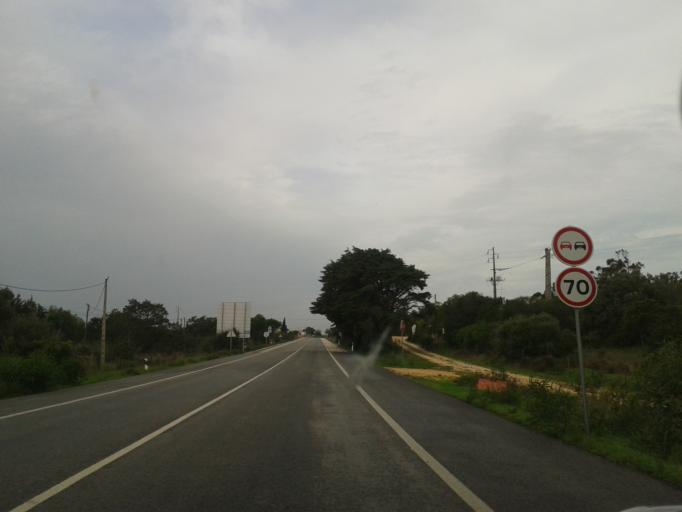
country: PT
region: Faro
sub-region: Vila do Bispo
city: Vila do Bispo
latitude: 37.0924
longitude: -8.7969
